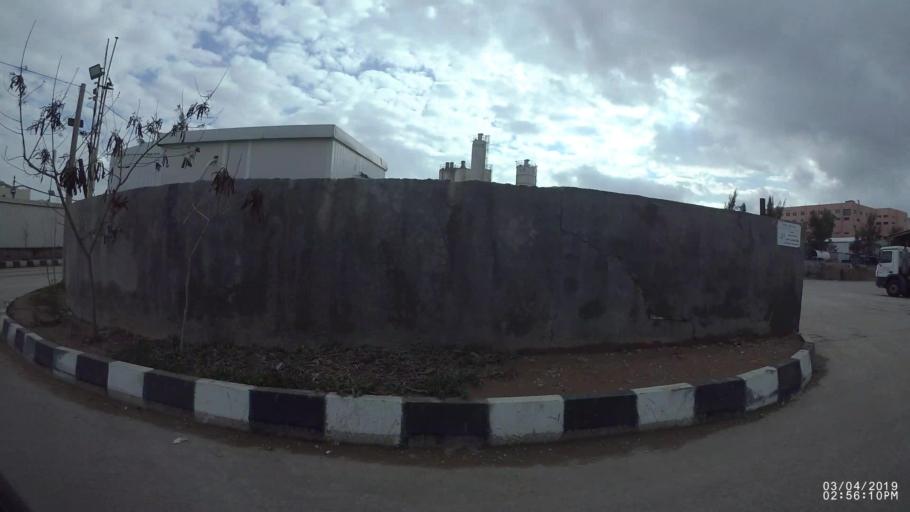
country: JO
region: Amman
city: Wadi as Sir
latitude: 31.9373
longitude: 35.8485
